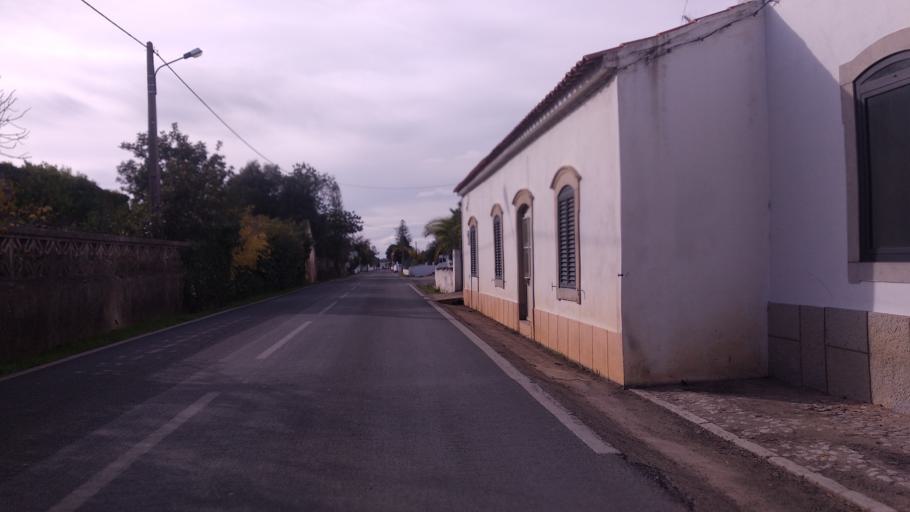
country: PT
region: Faro
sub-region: Sao Bras de Alportel
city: Sao Bras de Alportel
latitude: 37.1526
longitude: -7.9109
